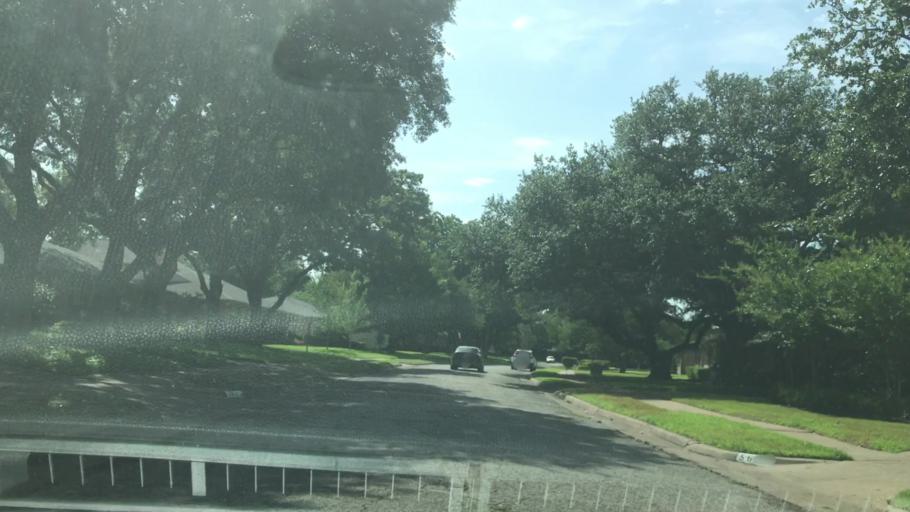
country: US
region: Texas
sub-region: Dallas County
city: Highland Park
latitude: 32.8536
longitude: -96.7554
